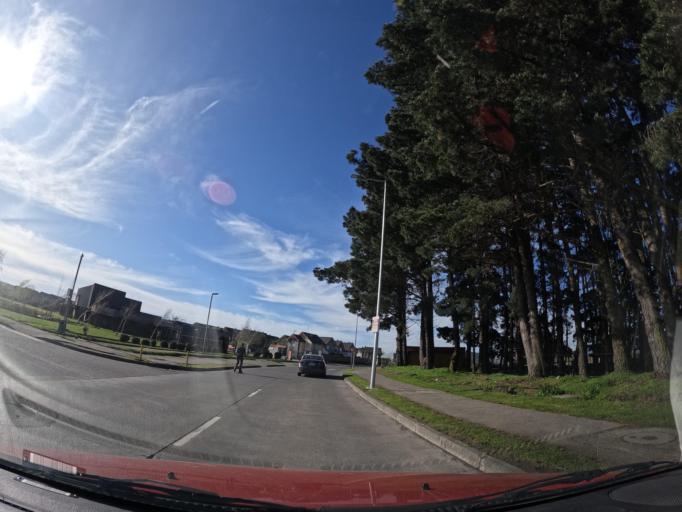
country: CL
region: Biobio
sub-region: Provincia de Concepcion
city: Concepcion
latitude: -36.7742
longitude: -73.0686
